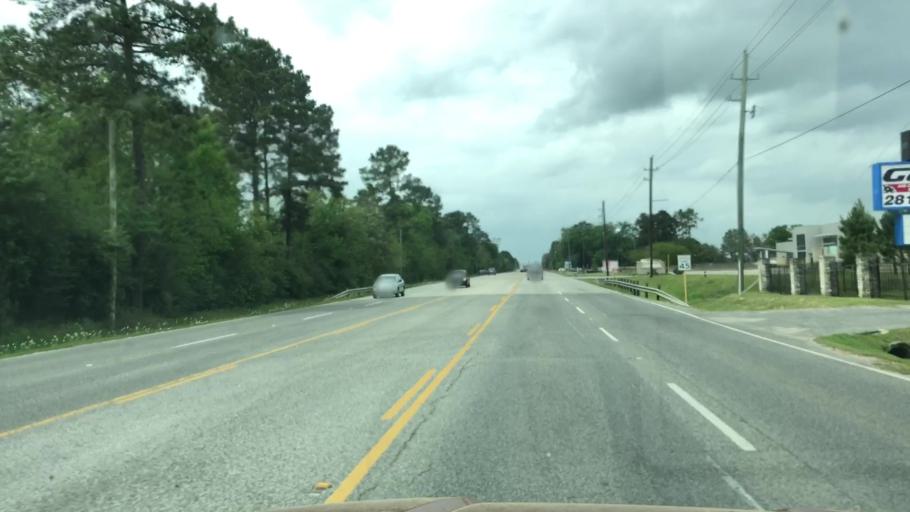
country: US
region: Texas
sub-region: Harris County
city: Spring
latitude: 30.0619
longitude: -95.4992
